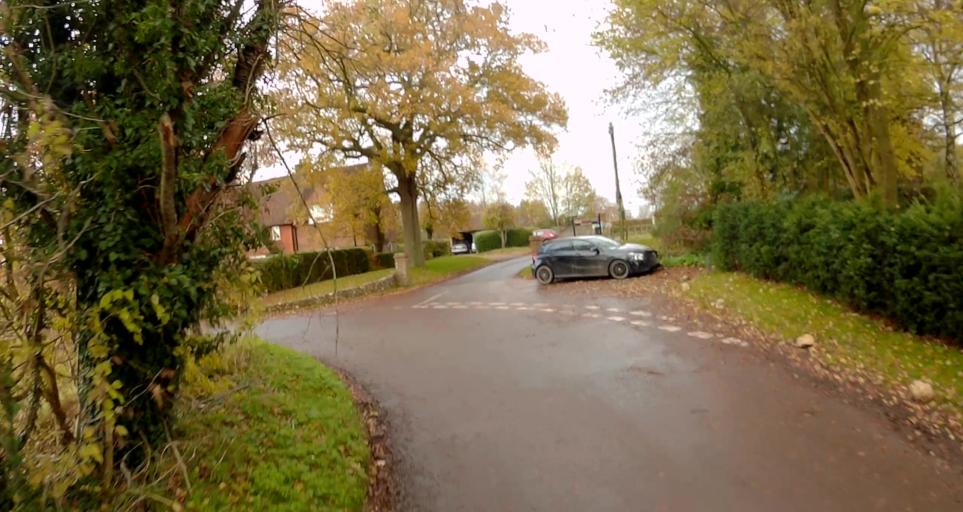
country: GB
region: England
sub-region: Hampshire
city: Long Sutton
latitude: 51.2084
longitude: -0.9402
